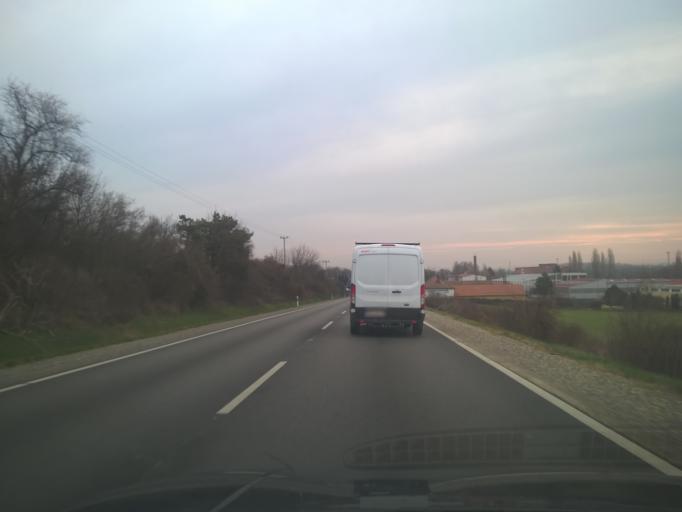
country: HU
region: Baranya
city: Pellerd
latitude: 46.0619
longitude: 18.1437
